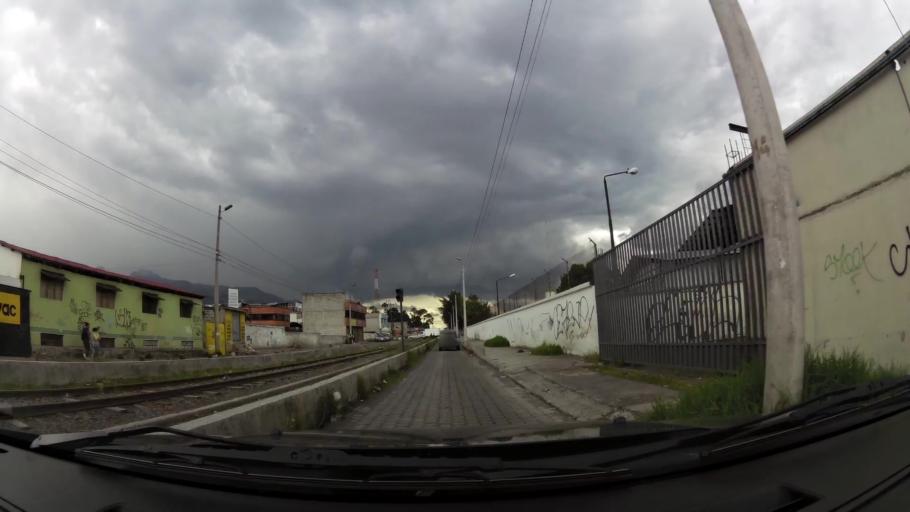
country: EC
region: Pichincha
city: Quito
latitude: -0.2772
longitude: -78.5338
